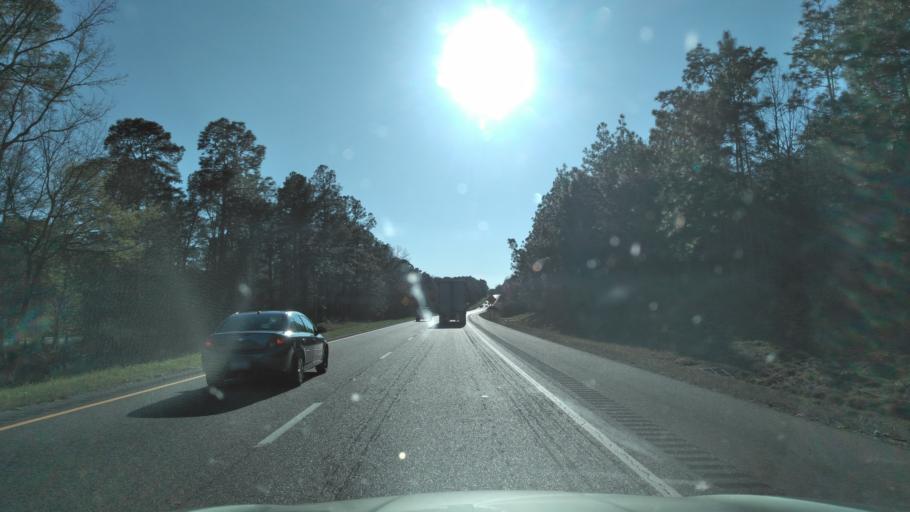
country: US
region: Alabama
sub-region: Escambia County
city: Atmore
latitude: 31.0660
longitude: -87.5622
